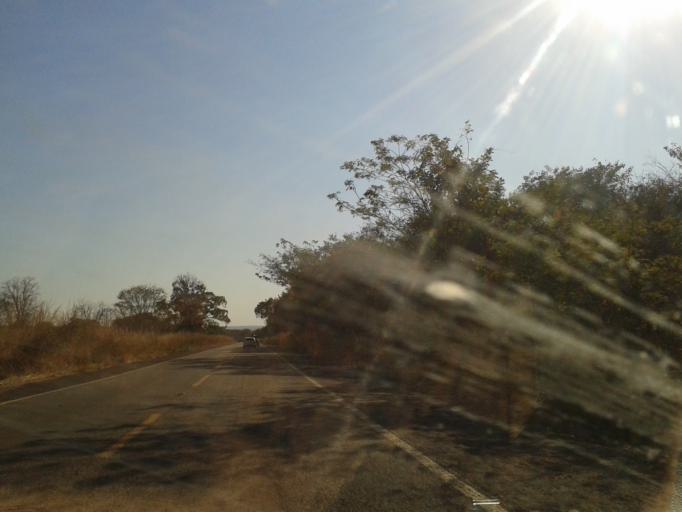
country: BR
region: Goias
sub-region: Mozarlandia
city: Mozarlandia
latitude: -15.0449
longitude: -50.6068
